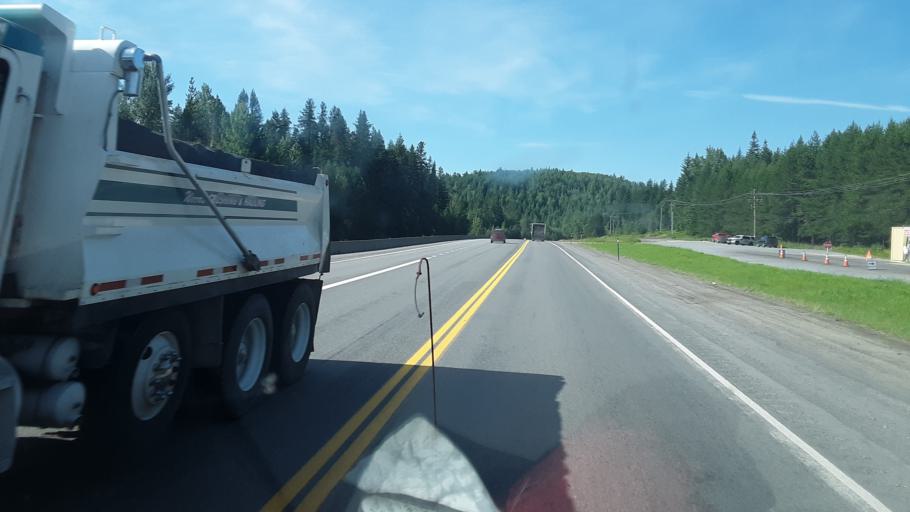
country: US
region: Idaho
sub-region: Bonner County
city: Ponderay
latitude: 48.4273
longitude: -116.4949
